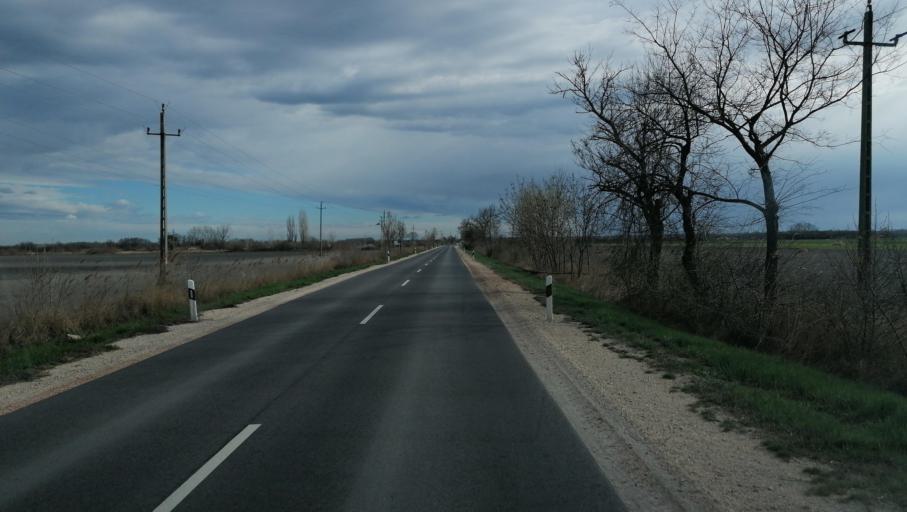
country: HU
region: Pest
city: Bugyi
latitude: 47.2384
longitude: 19.1894
